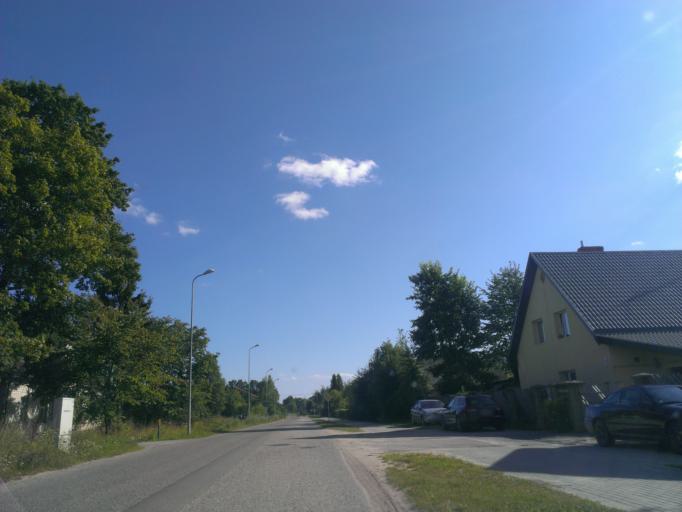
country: LV
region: Sigulda
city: Sigulda
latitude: 57.1613
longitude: 24.8882
